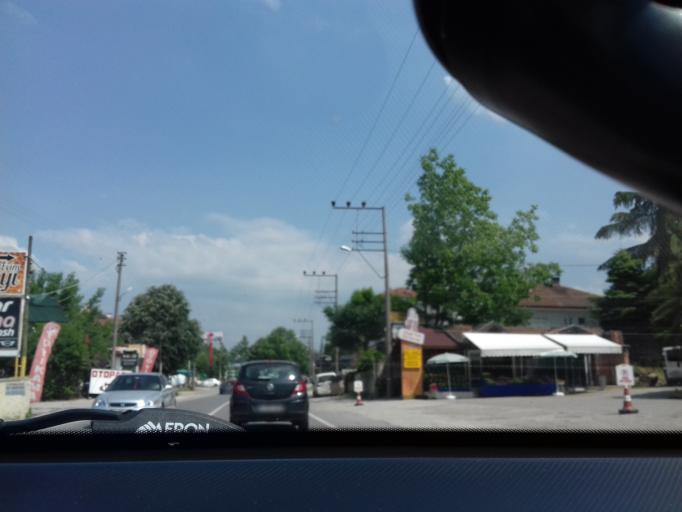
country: TR
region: Sakarya
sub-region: Merkez
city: Sapanca
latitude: 40.6898
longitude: 30.2325
